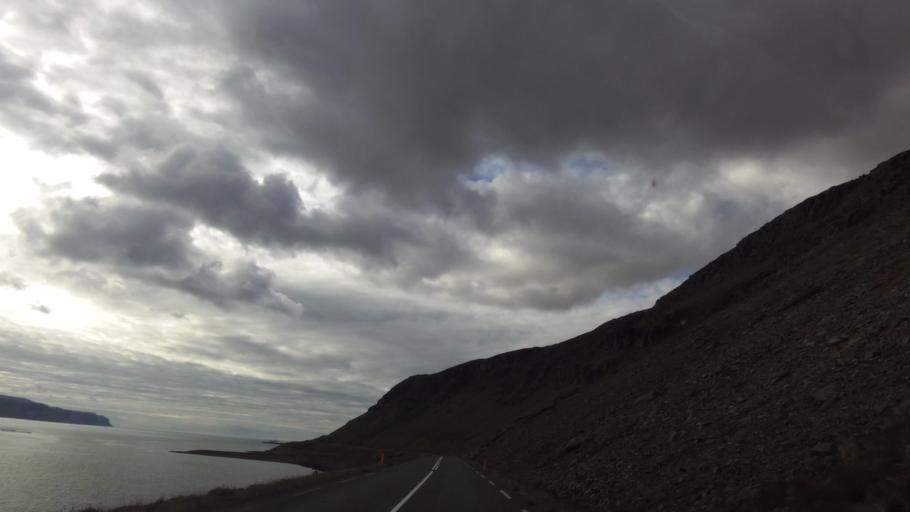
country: IS
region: West
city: Olafsvik
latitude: 65.5756
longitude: -23.9430
